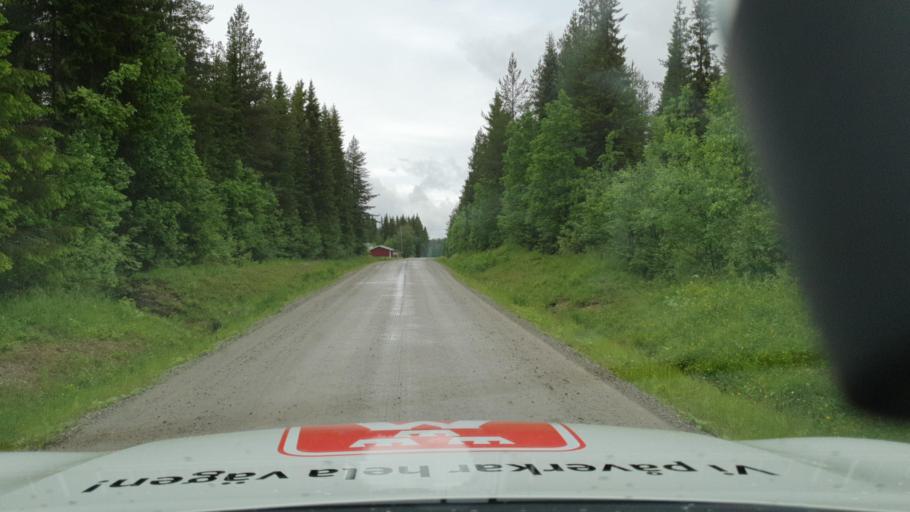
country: SE
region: Vaesterbotten
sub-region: Dorotea Kommun
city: Dorotea
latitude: 64.0720
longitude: 16.6941
